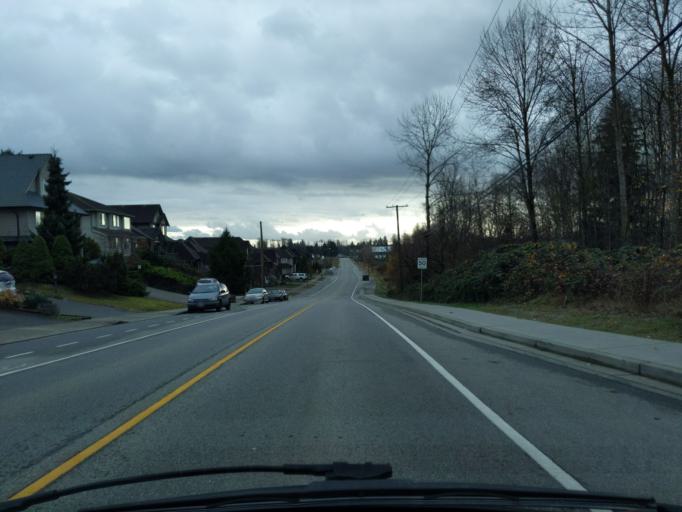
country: CA
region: British Columbia
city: Pitt Meadows
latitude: 49.2151
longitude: -122.6896
